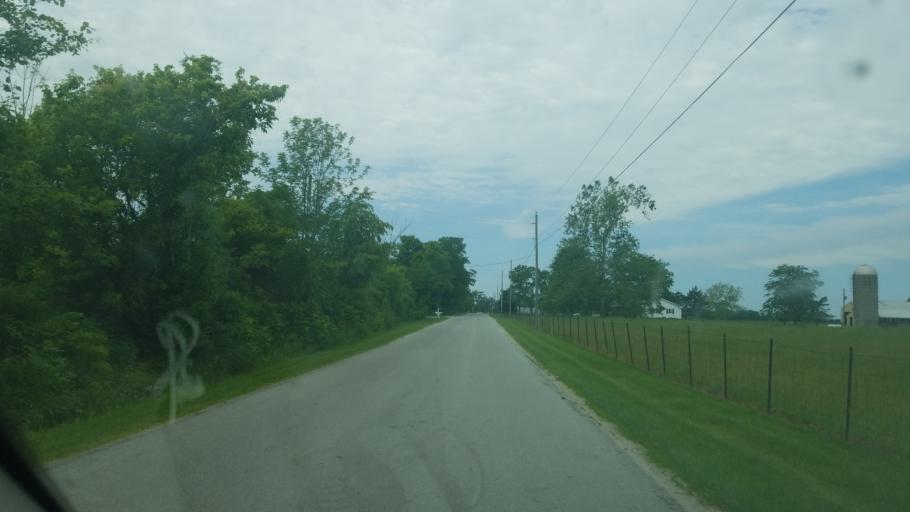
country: US
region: Ohio
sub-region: Wood County
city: North Baltimore
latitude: 41.2220
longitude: -83.6349
